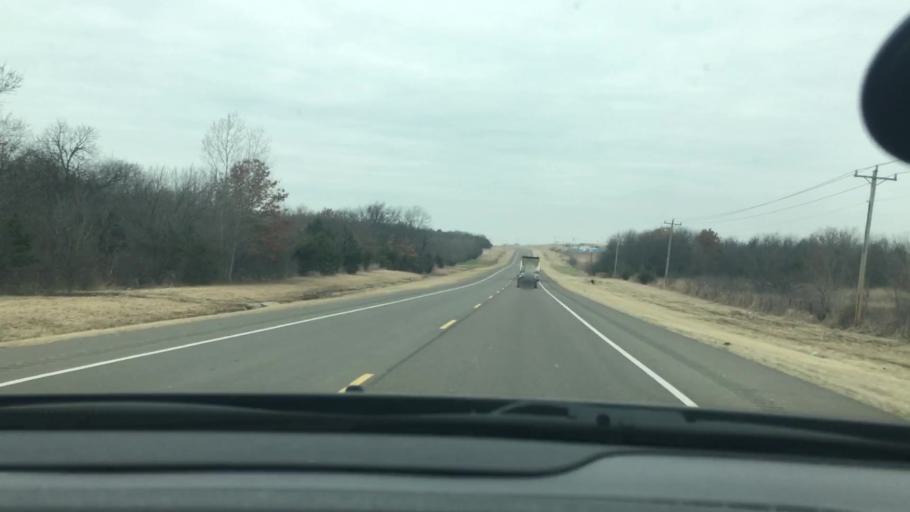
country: US
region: Oklahoma
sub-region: Murray County
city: Davis
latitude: 34.5150
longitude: -97.2034
